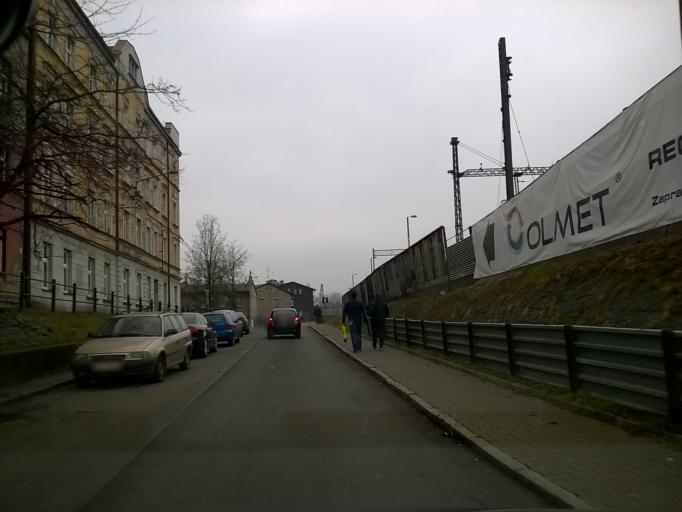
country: PL
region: Silesian Voivodeship
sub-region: Swietochlowice
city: Swietochlowice
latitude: 50.2762
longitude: 18.9484
